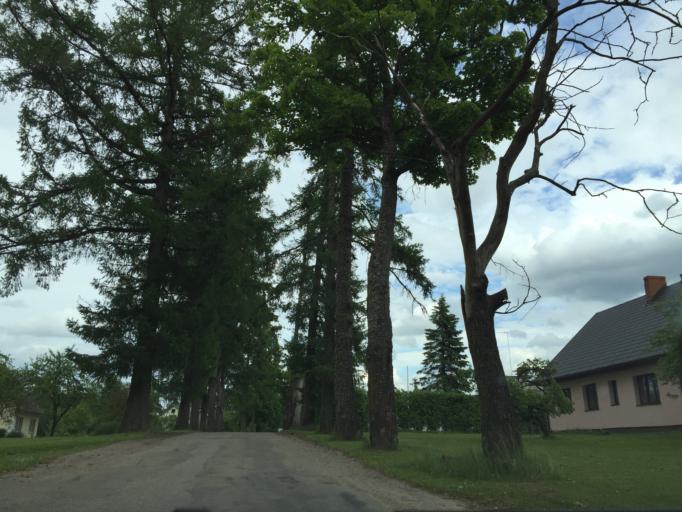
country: LV
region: Apes Novads
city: Ape
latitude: 57.4227
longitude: 26.3575
